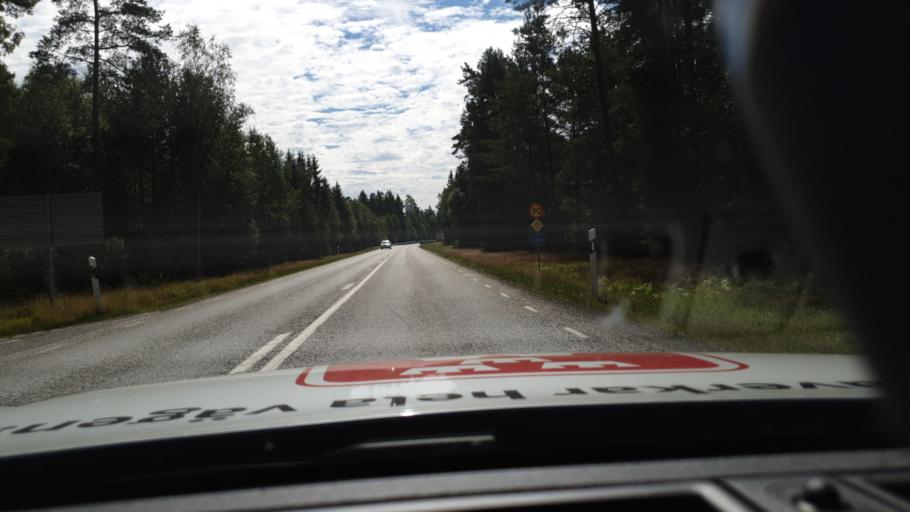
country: SE
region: Joenkoeping
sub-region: Jonkopings Kommun
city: Odensjo
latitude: 57.6087
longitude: 14.2139
